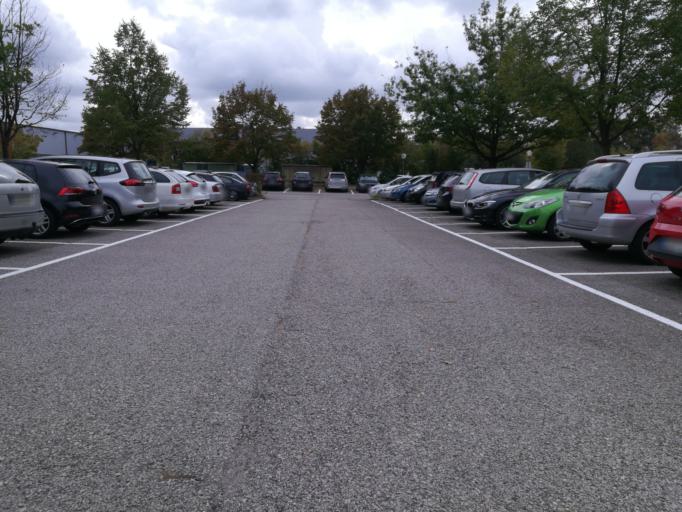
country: DE
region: Bavaria
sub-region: Regierungsbezirk Mittelfranken
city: Nuernberg
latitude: 49.4804
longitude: 11.1242
